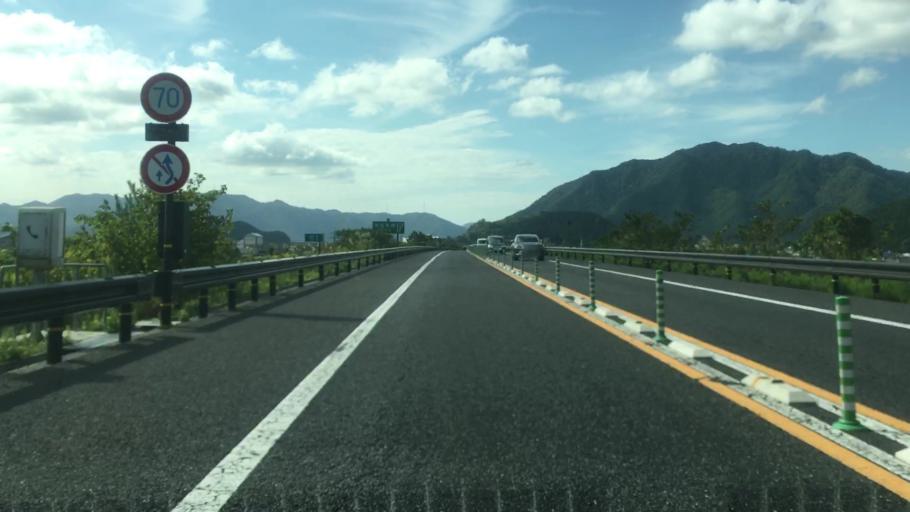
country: JP
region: Kyoto
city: Fukuchiyama
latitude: 35.1907
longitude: 135.0416
